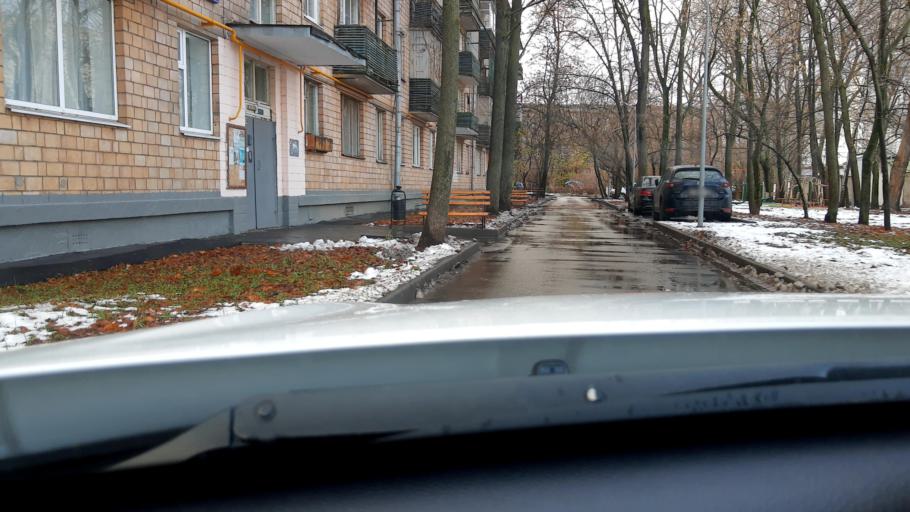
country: RU
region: Moskovskaya
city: Dorogomilovo
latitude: 55.7712
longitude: 37.5588
